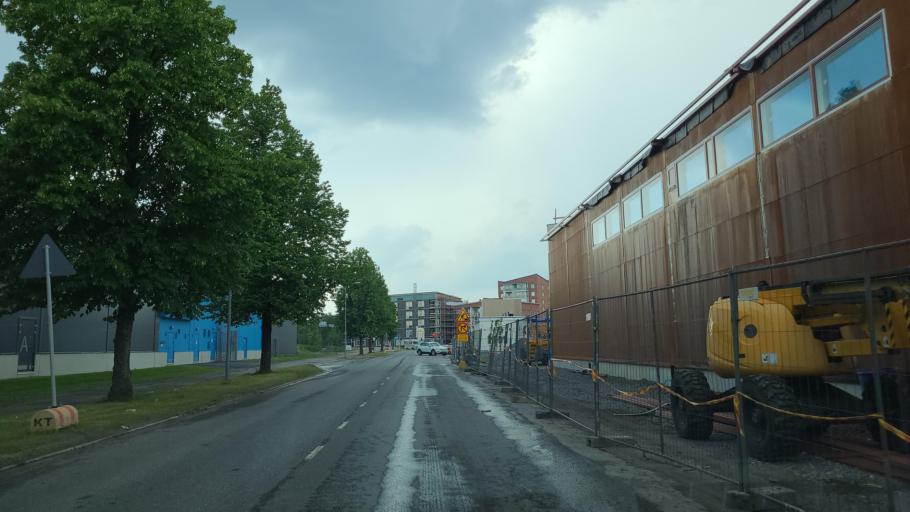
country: FI
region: Ostrobothnia
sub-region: Vaasa
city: Vaasa
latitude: 63.0985
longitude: 21.6358
